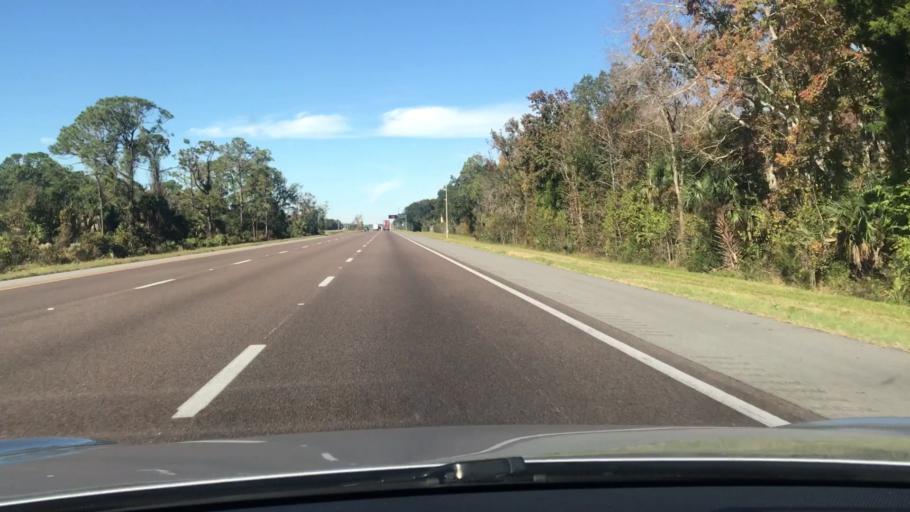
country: US
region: Florida
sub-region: Volusia County
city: Edgewater
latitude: 28.9335
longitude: -80.9424
